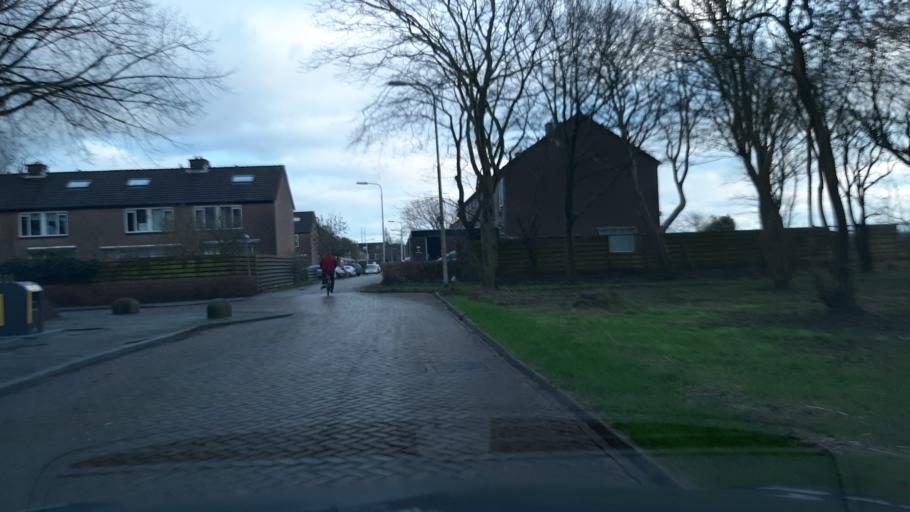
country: NL
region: South Holland
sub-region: Gemeente Hillegom
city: Hillegom
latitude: 52.2802
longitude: 4.5805
